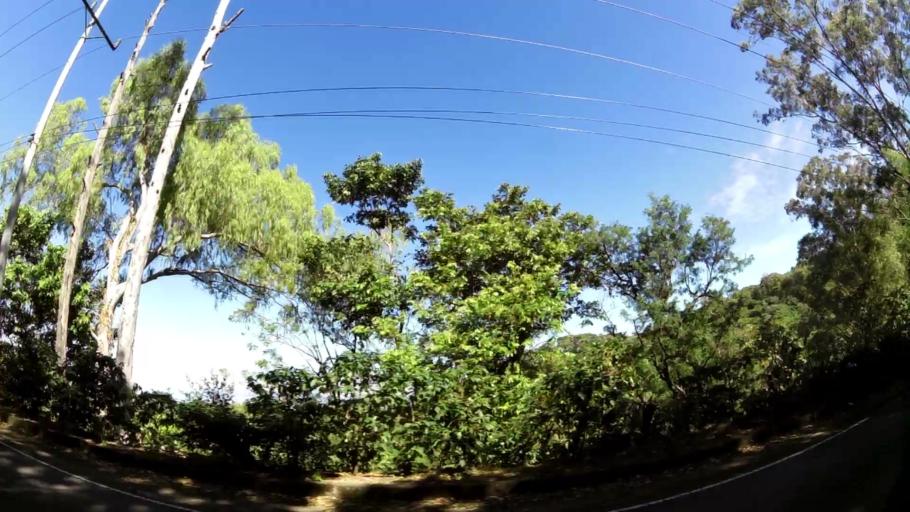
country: SV
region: Ahuachapan
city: Concepcion de Ataco
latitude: 13.8871
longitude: -89.8426
